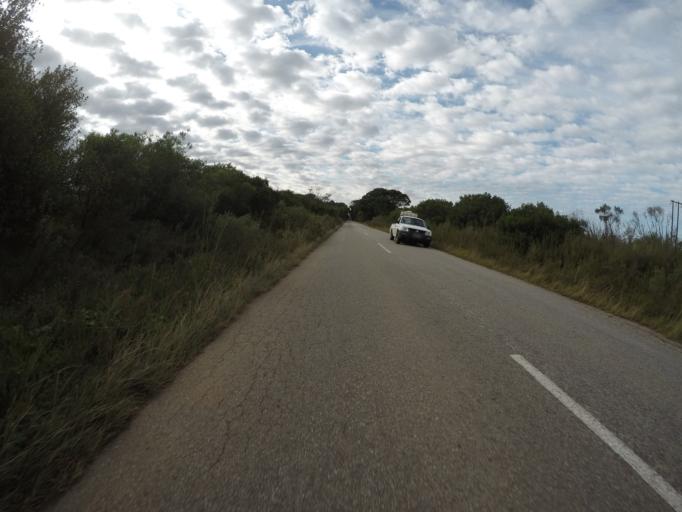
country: ZA
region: Eastern Cape
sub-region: Cacadu District Municipality
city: Kareedouw
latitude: -34.0456
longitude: 24.4484
